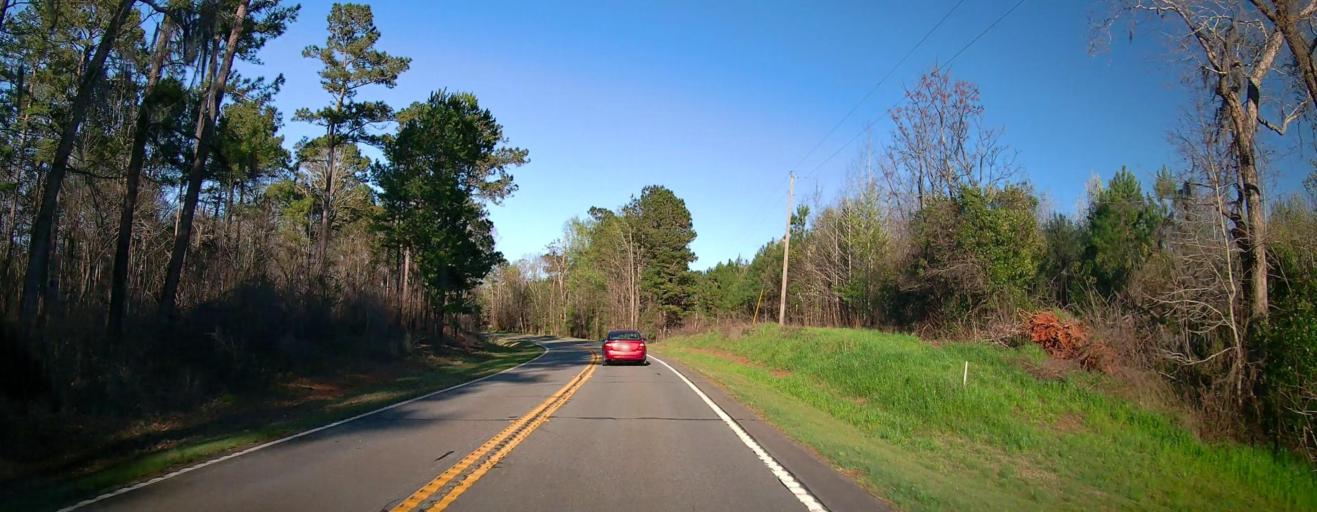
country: US
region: Georgia
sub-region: Pulaski County
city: Hawkinsville
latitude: 32.2559
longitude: -83.5675
